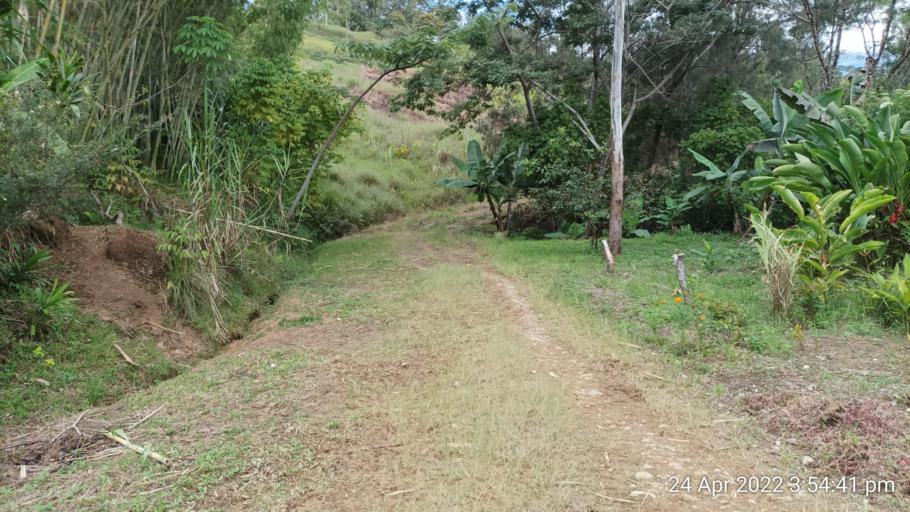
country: PG
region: Jiwaka
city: Minj
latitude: -5.8986
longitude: 144.8234
